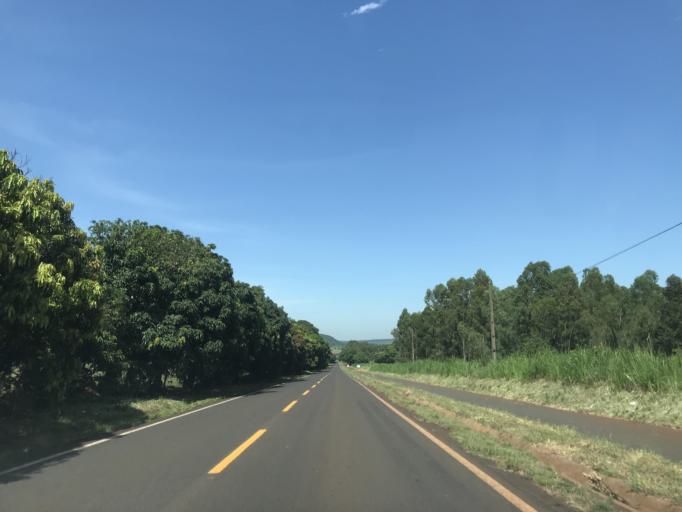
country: BR
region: Parana
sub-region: Terra Rica
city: Terra Rica
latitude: -22.7561
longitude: -52.6295
